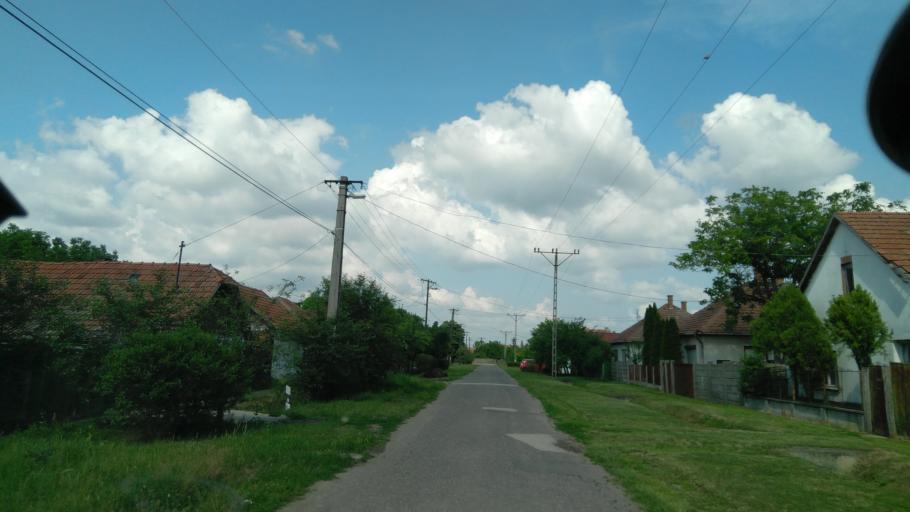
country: HU
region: Bekes
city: Doboz
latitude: 46.7295
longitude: 21.2457
